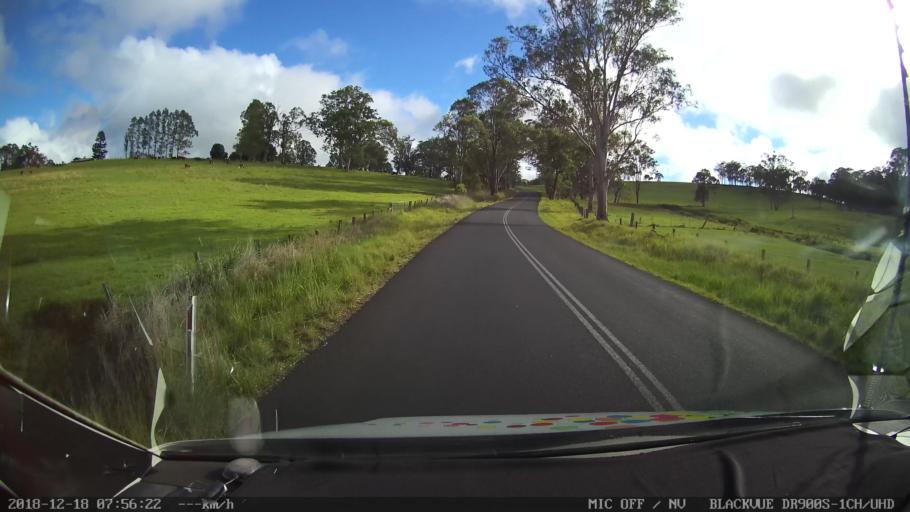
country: AU
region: New South Wales
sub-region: Kyogle
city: Kyogle
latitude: -28.3995
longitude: 152.6058
